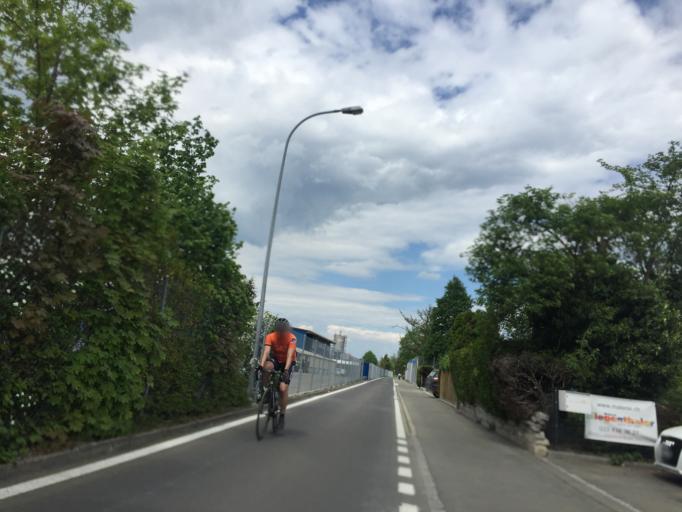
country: CH
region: Bern
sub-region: Thun District
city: Thun
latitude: 46.7681
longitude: 7.6178
